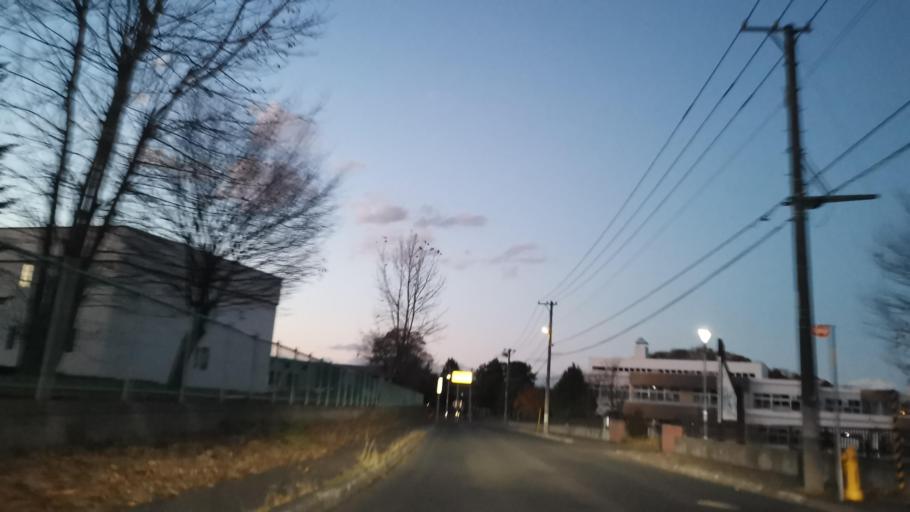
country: JP
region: Hokkaido
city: Sapporo
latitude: 42.9995
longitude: 141.3638
